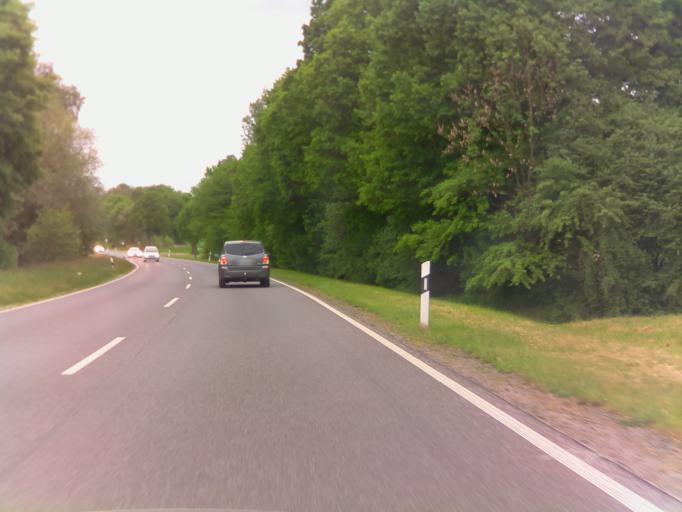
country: DE
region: Hesse
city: Neustadt (Hessen)
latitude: 50.8447
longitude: 9.0795
